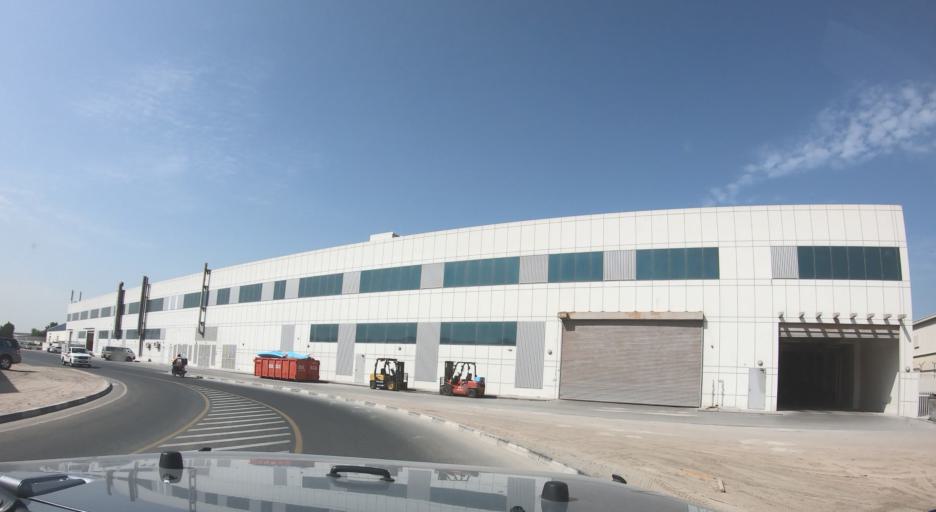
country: AE
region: Dubai
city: Dubai
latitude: 25.1531
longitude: 55.2346
